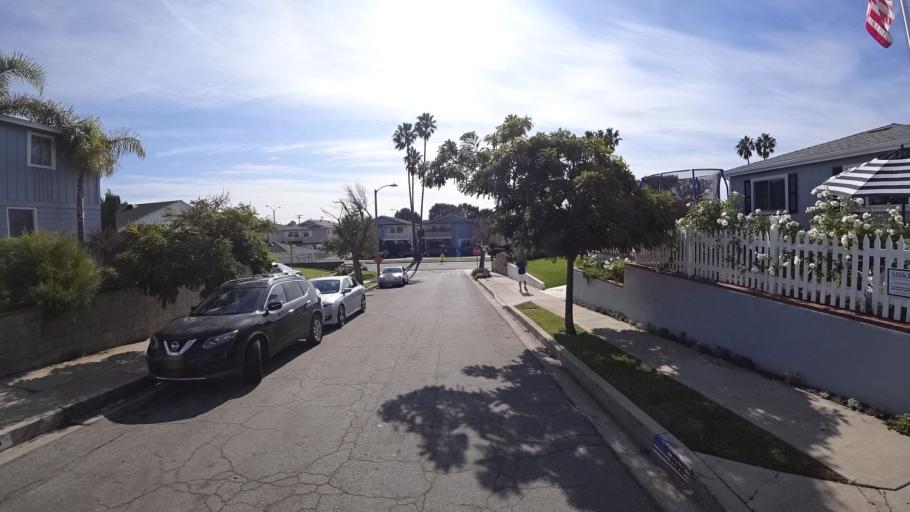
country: US
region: California
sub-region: Los Angeles County
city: Manhattan Beach
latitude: 33.8879
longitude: -118.3925
